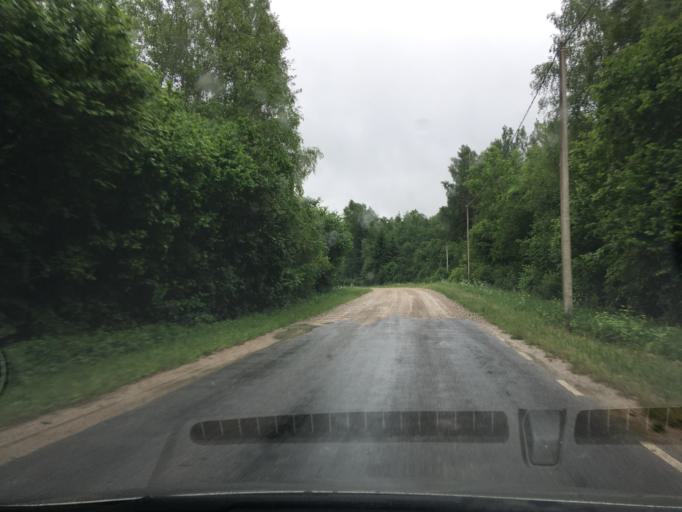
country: EE
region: Laeaene
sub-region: Lihula vald
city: Lihula
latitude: 58.6502
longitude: 23.7750
